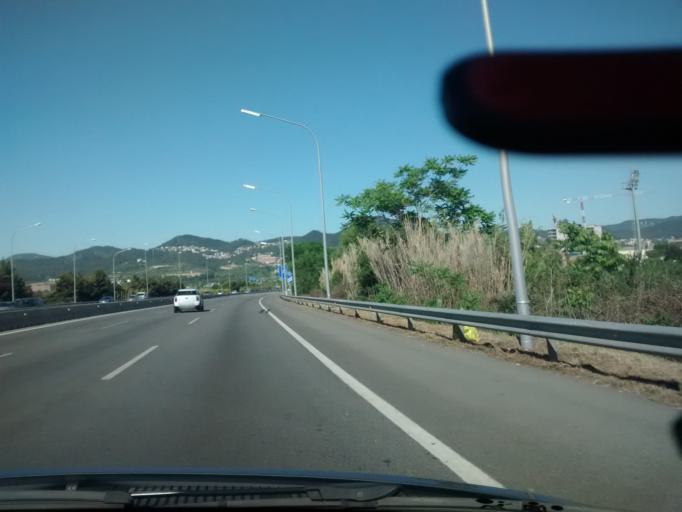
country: ES
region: Catalonia
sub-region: Provincia de Barcelona
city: Sant Feliu de Llobregat
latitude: 41.3735
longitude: 2.0542
